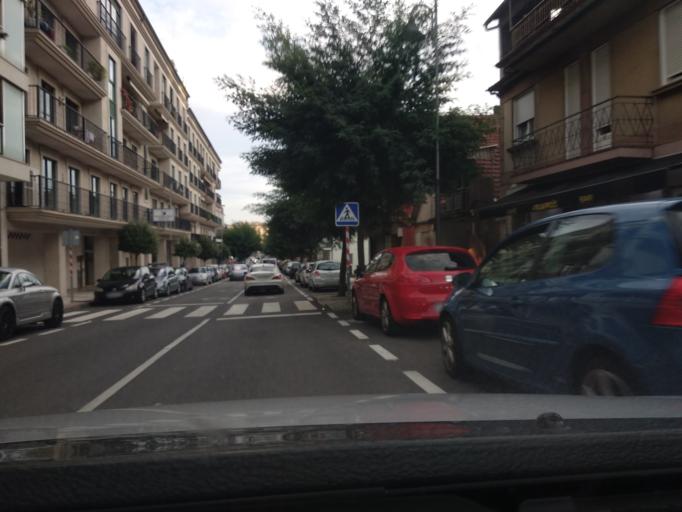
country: ES
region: Galicia
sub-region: Provincia de Pontevedra
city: Moana
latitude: 42.2886
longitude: -8.7354
